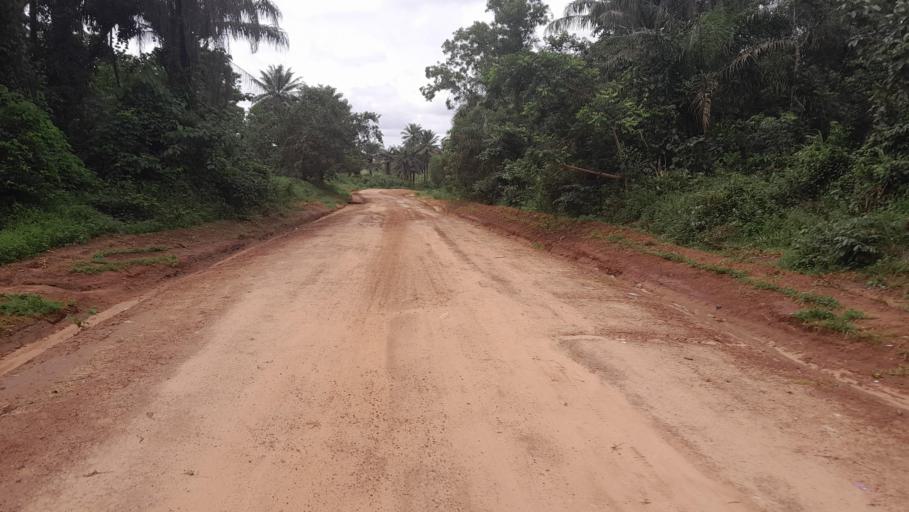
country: GN
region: Boke
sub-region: Boffa
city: Boffa
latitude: 10.1001
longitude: -13.8556
